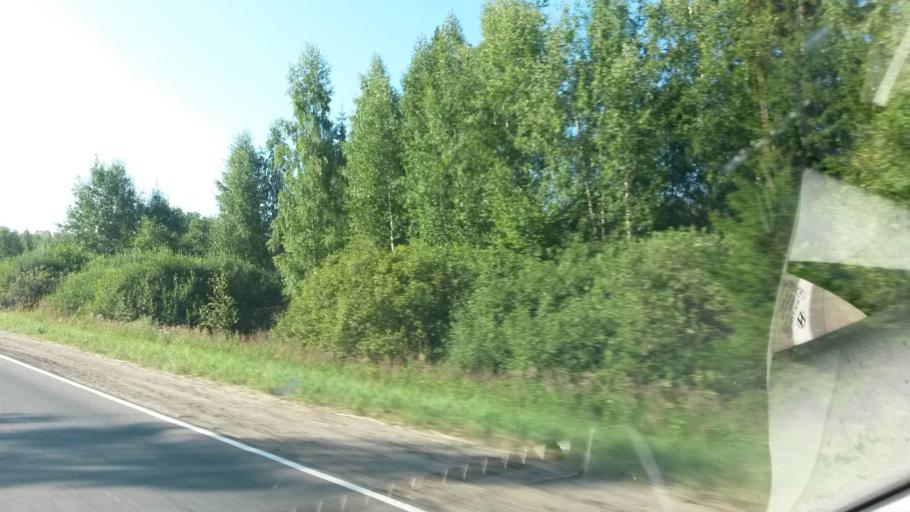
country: RU
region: Ivanovo
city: Pistsovo
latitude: 57.0978
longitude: 40.6579
